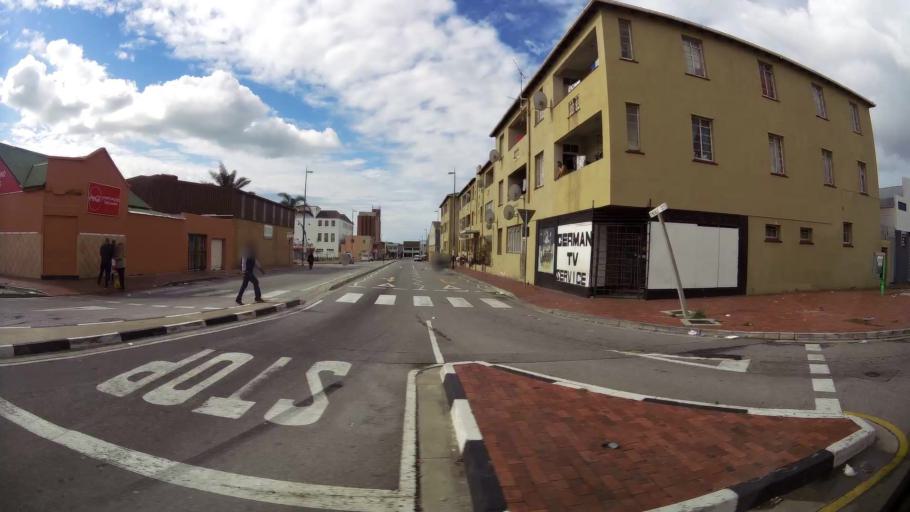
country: ZA
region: Eastern Cape
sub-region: Nelson Mandela Bay Metropolitan Municipality
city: Port Elizabeth
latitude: -33.9429
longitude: 25.6028
